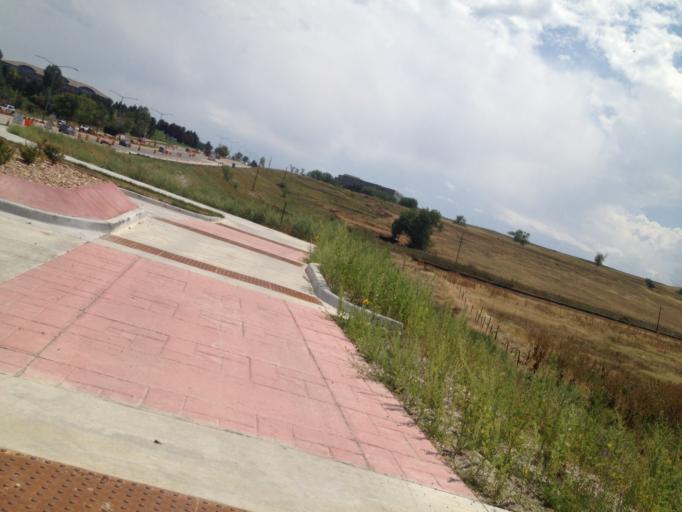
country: US
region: Colorado
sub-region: Boulder County
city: Superior
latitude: 39.9518
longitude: -105.1656
